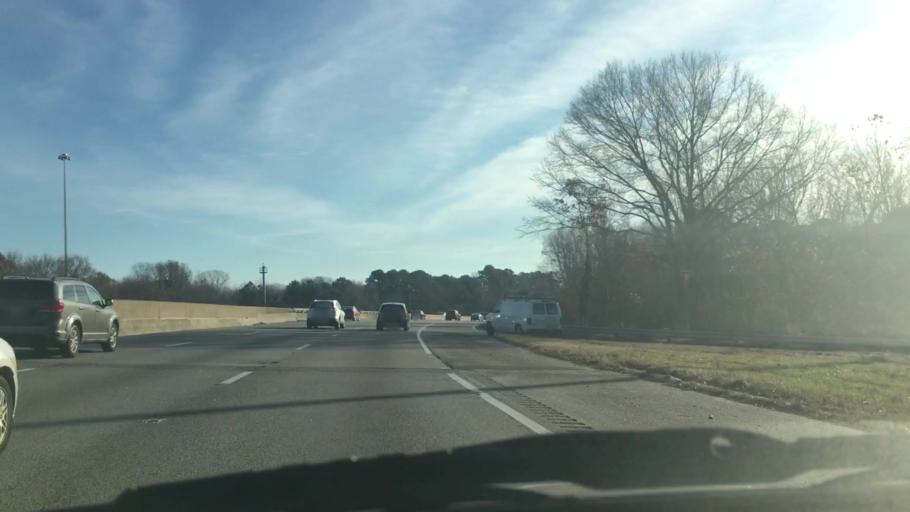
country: US
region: Virginia
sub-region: City of Norfolk
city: Norfolk
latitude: 36.9033
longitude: -76.2408
